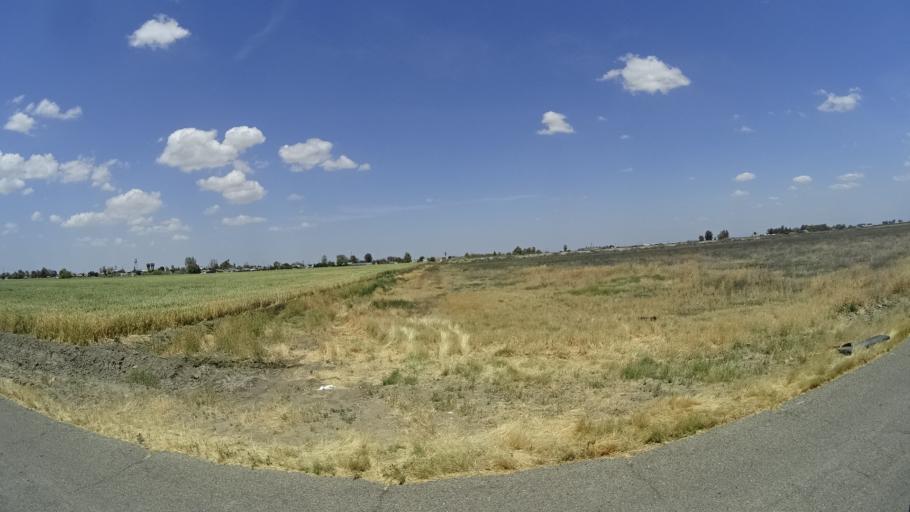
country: US
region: California
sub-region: Kings County
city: Stratford
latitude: 36.1821
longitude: -119.8201
